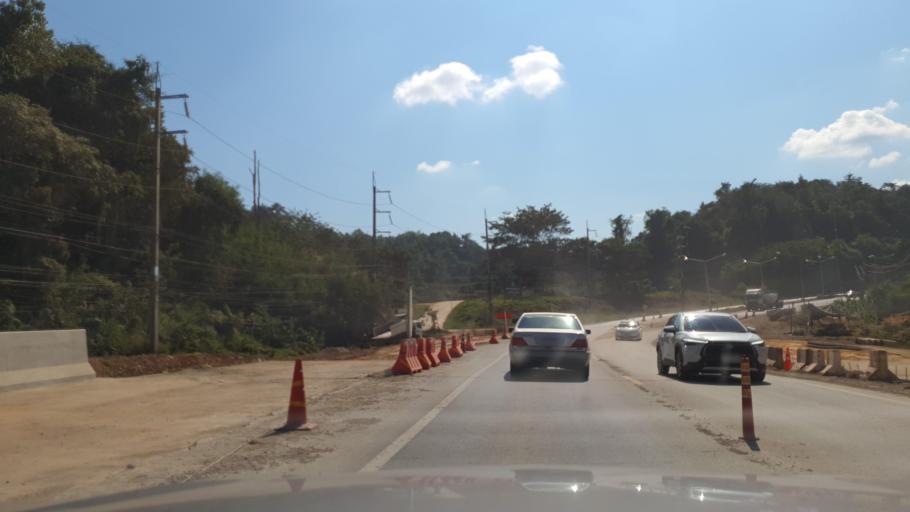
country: TH
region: Nan
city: Nan
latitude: 18.9199
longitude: 100.7658
